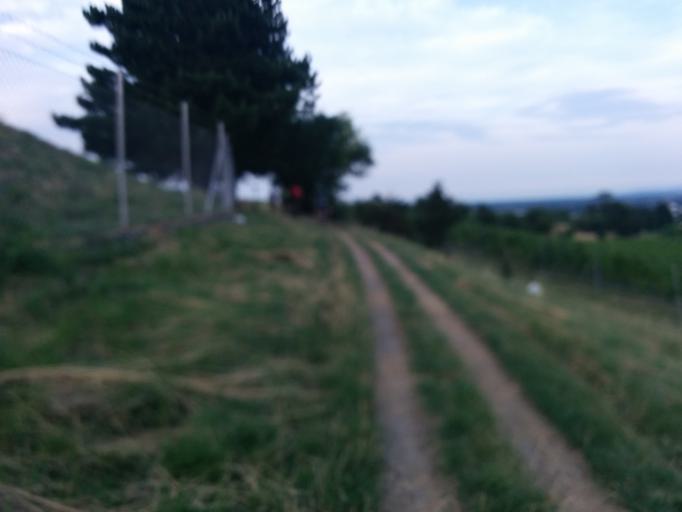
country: AT
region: Lower Austria
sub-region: Politischer Bezirk Modling
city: Gumpoldskirchen
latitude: 48.0546
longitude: 16.2901
